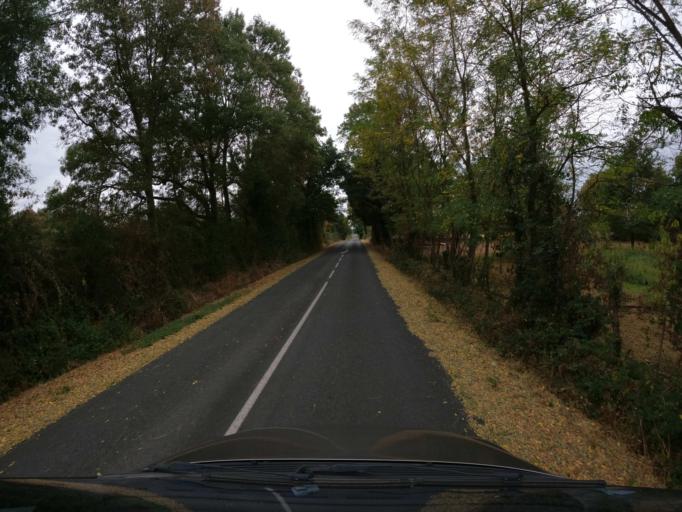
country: FR
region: Pays de la Loire
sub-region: Departement de la Vendee
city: Tiffauges
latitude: 47.0068
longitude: -1.1092
